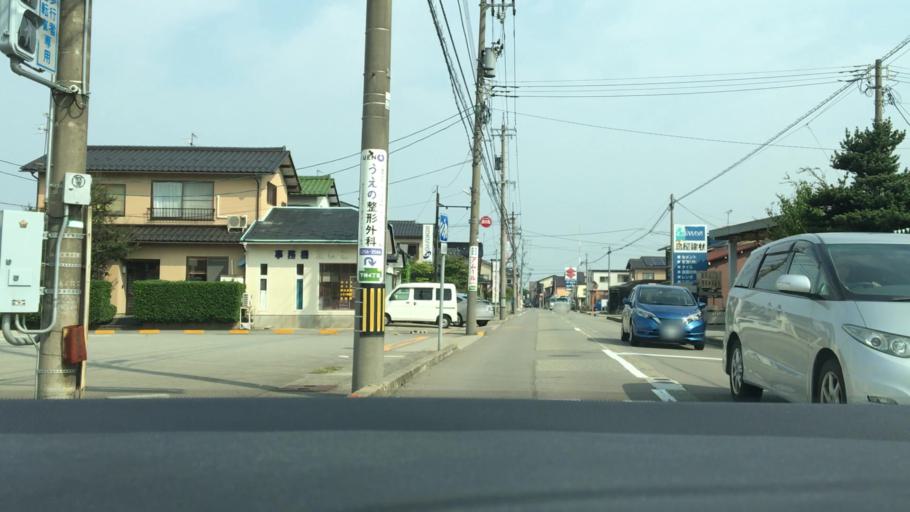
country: JP
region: Ishikawa
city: Nonoichi
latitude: 36.5234
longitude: 136.6042
